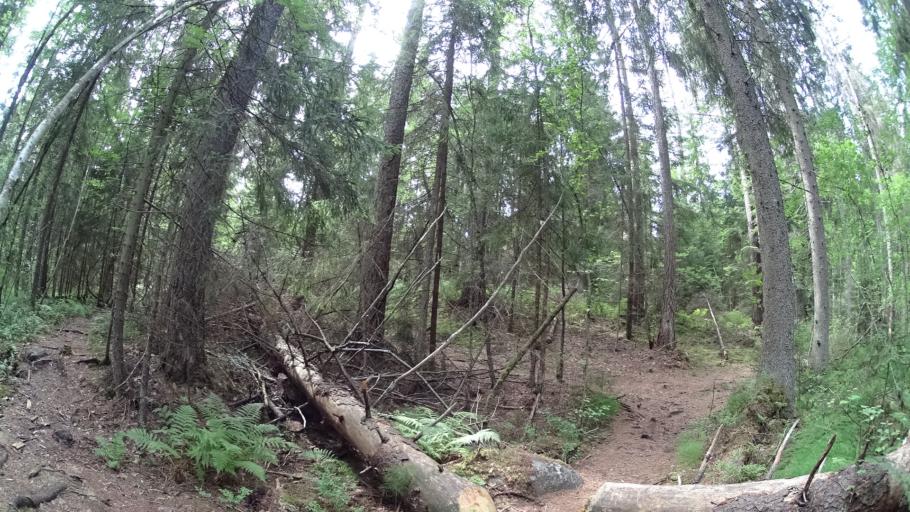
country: FI
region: Uusimaa
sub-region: Helsinki
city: Espoo
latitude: 60.1995
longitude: 24.6176
